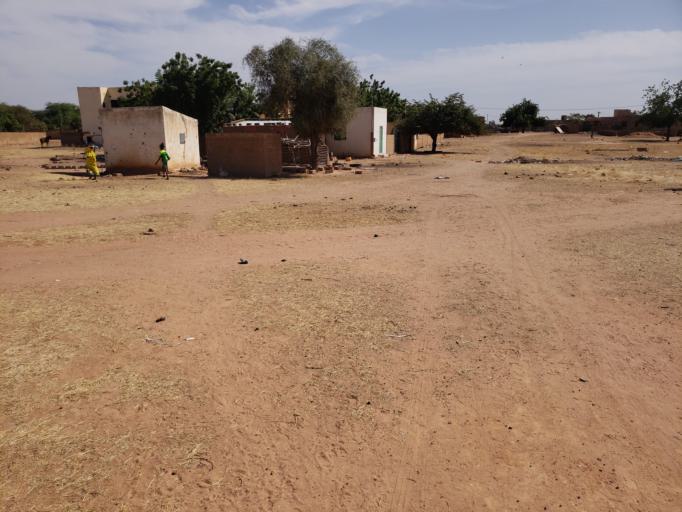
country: SN
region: Matam
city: Ranerou
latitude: 15.2976
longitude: -13.9655
